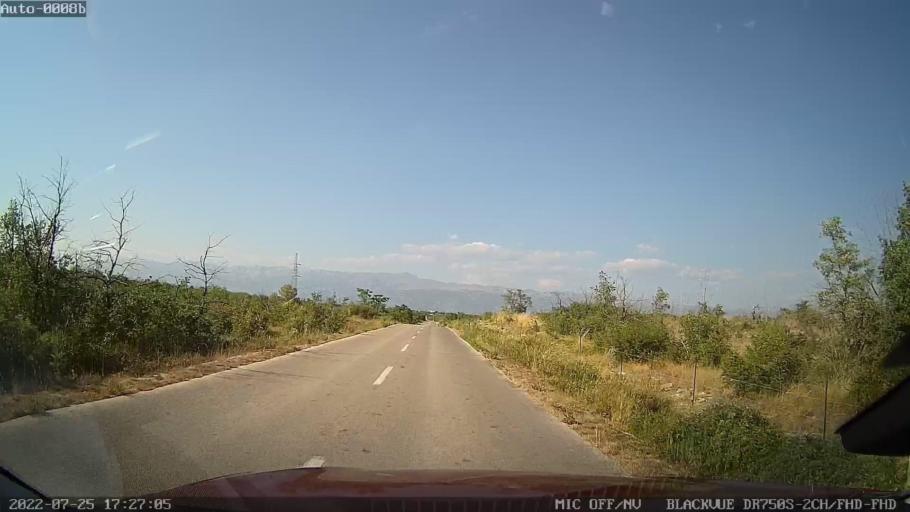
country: HR
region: Zadarska
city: Pridraga
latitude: 44.1397
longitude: 15.5031
